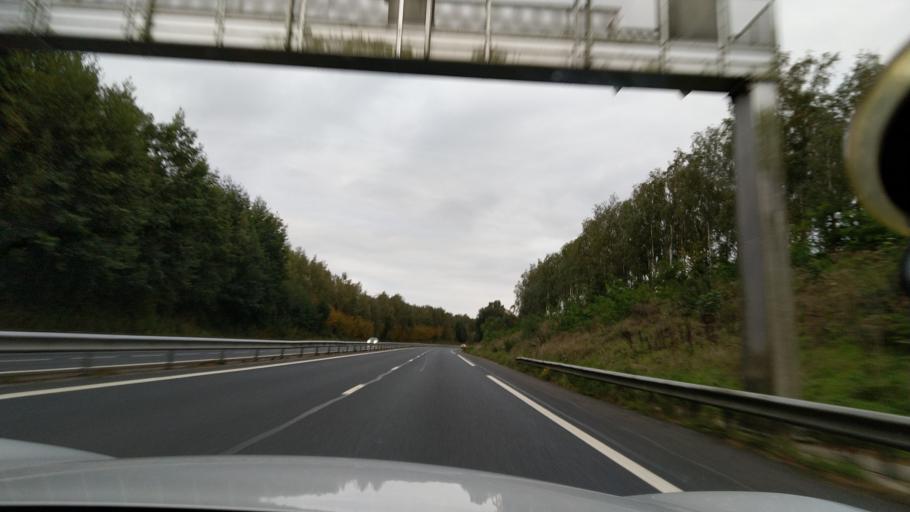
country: FR
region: Haute-Normandie
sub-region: Departement de la Seine-Maritime
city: Saint-Martin-Osmonville
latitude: 49.6428
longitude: 1.2667
